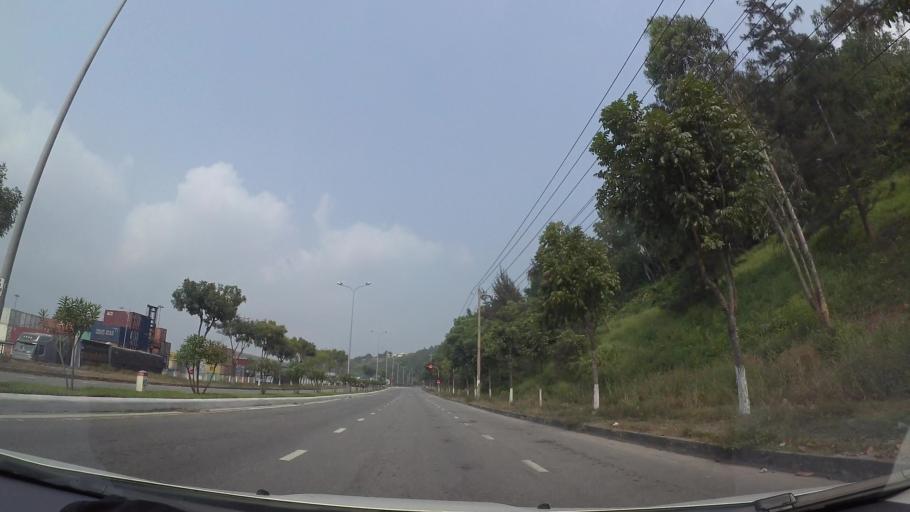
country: VN
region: Da Nang
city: Da Nang
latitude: 16.1167
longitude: 108.2321
